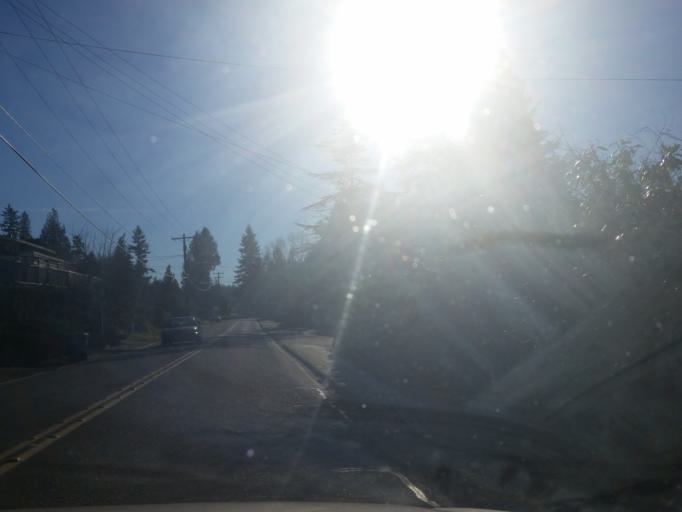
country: US
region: Washington
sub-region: Snohomish County
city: Edmonds
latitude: 47.8255
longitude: -122.3618
